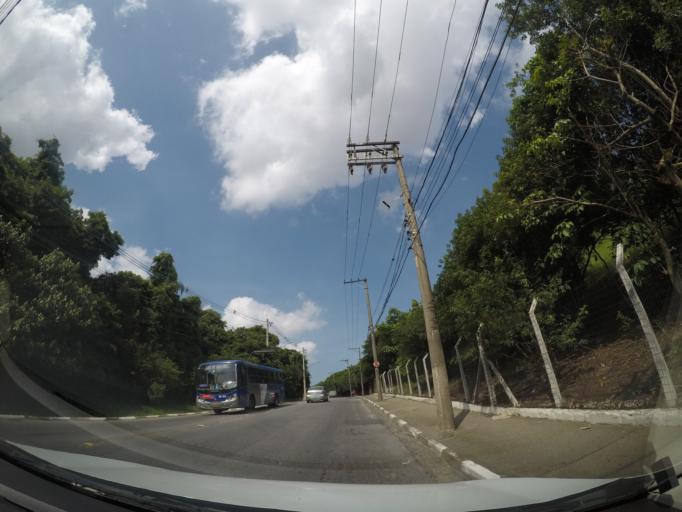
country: BR
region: Sao Paulo
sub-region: Guarulhos
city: Guarulhos
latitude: -23.4577
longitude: -46.4884
